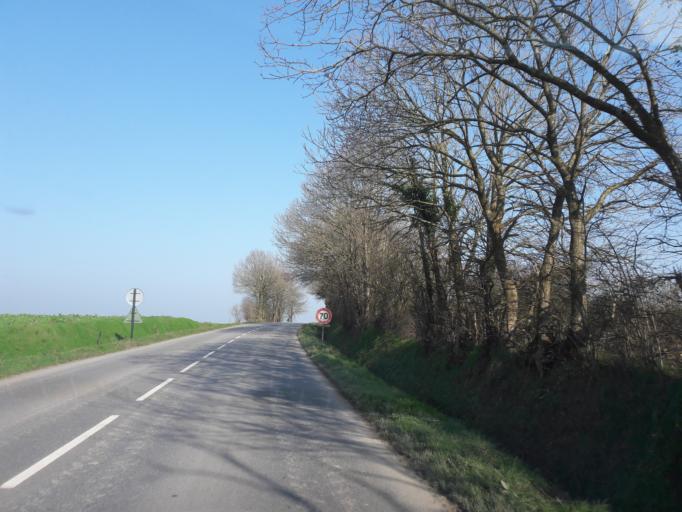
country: FR
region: Brittany
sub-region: Departement d'Ille-et-Vilaine
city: Corps-Nuds
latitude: 47.9350
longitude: -1.5589
